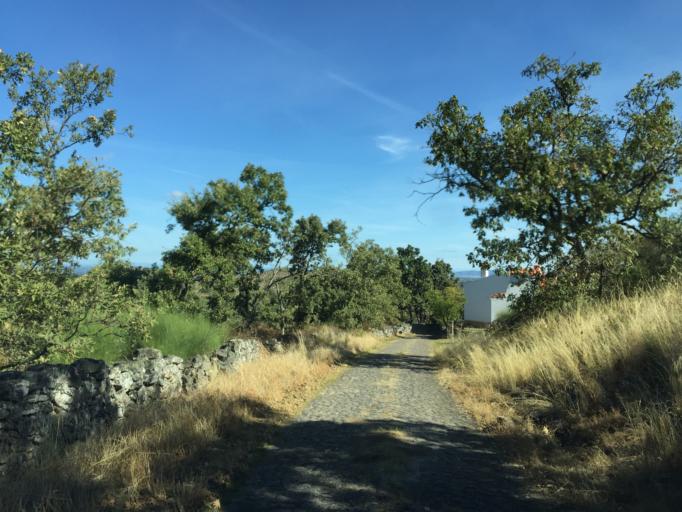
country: PT
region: Portalegre
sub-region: Marvao
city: Marvao
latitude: 39.4013
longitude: -7.3654
